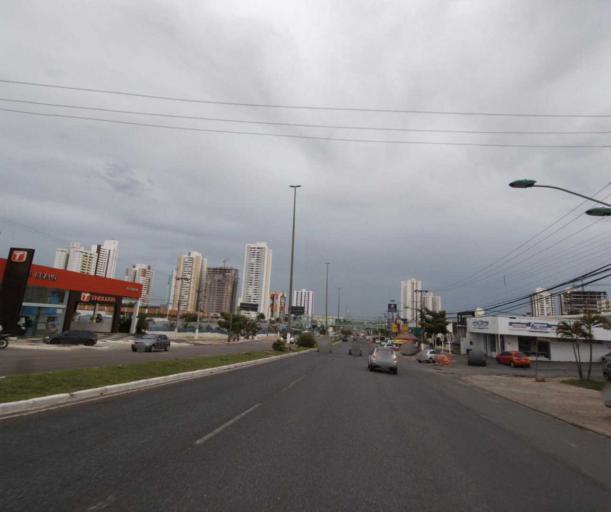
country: BR
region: Mato Grosso
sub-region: Cuiaba
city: Cuiaba
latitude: -15.6087
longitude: -56.0799
